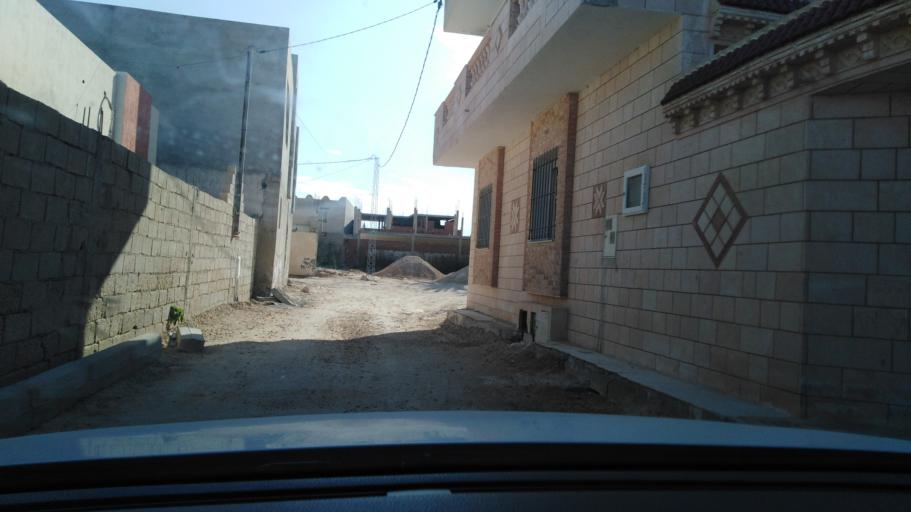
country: TN
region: Qabis
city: Gabes
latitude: 33.9418
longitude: 10.0712
